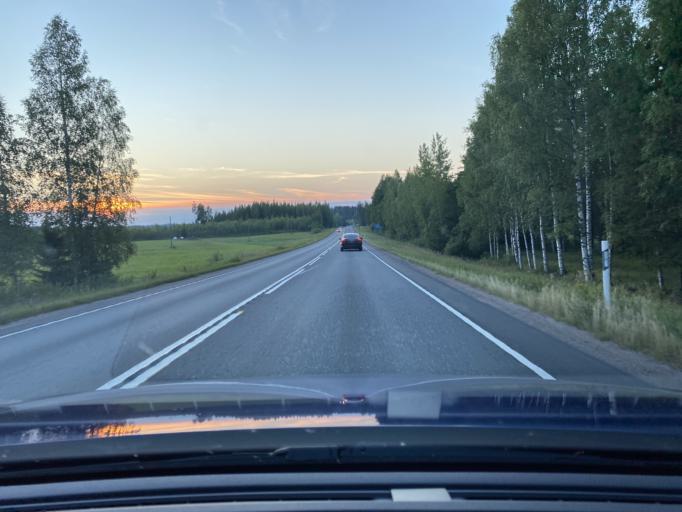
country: FI
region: Pirkanmaa
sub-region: Luoteis-Pirkanmaa
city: Ikaalinen
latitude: 61.8406
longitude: 22.9351
